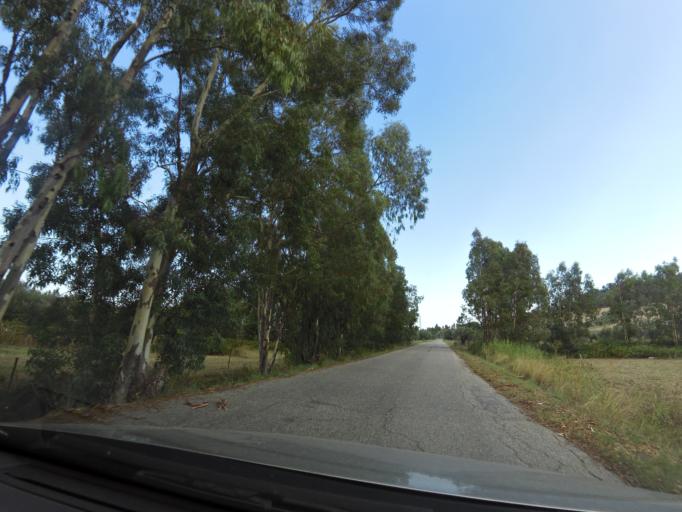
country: IT
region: Calabria
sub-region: Provincia di Reggio Calabria
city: Monasterace
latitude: 38.4274
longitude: 16.5297
